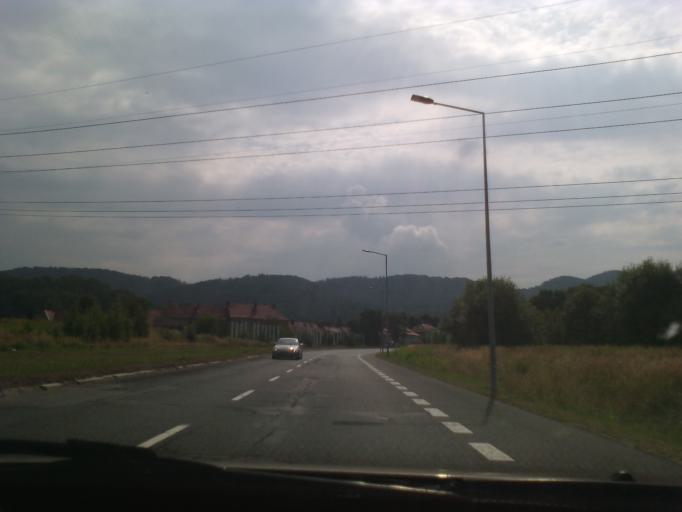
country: PL
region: Lower Silesian Voivodeship
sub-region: Powiat walbrzyski
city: Walbrzych
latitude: 50.7527
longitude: 16.2899
